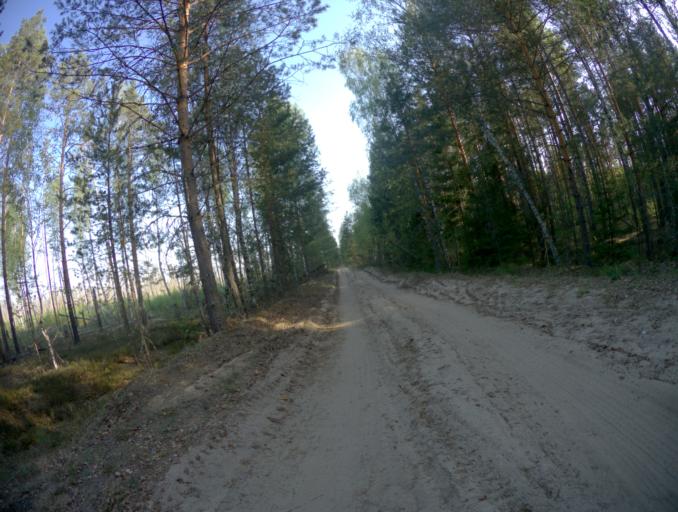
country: RU
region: Vladimir
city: Vyazniki
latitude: 56.4028
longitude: 42.1716
